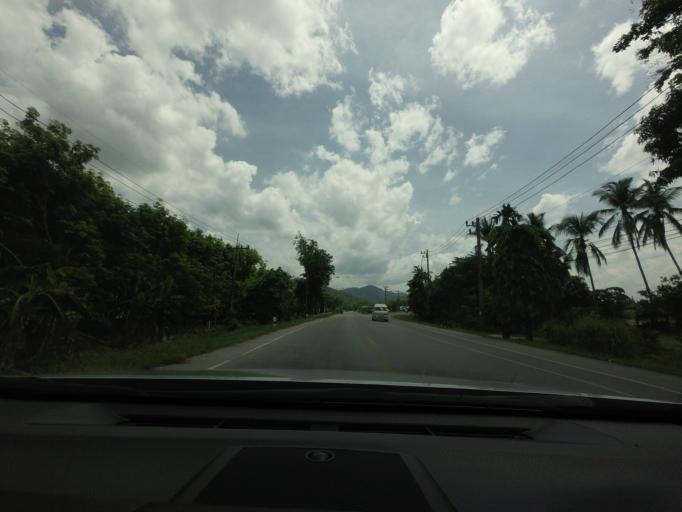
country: TH
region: Yala
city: Raman
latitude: 6.4560
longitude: 101.3585
